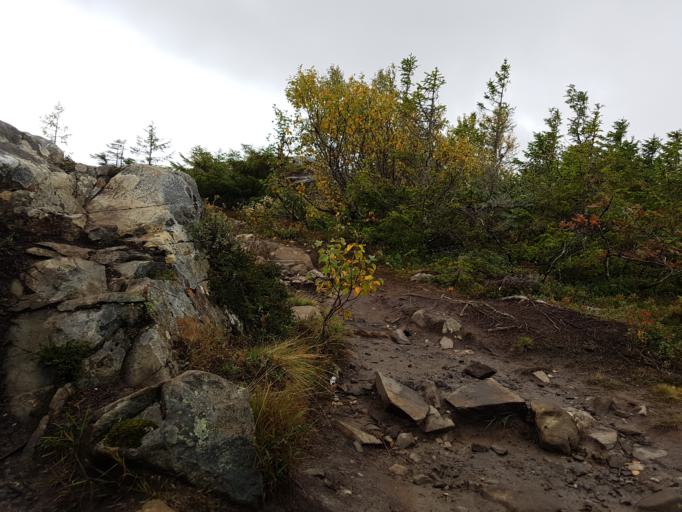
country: NO
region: Sor-Trondelag
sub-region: Melhus
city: Melhus
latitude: 63.4041
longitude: 10.2028
